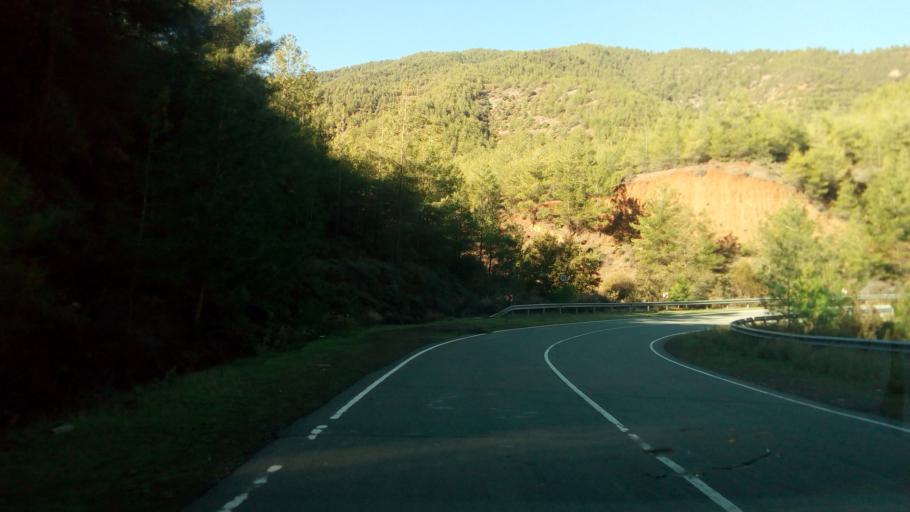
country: CY
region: Lefkosia
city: Lefka
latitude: 35.0891
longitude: 32.7583
